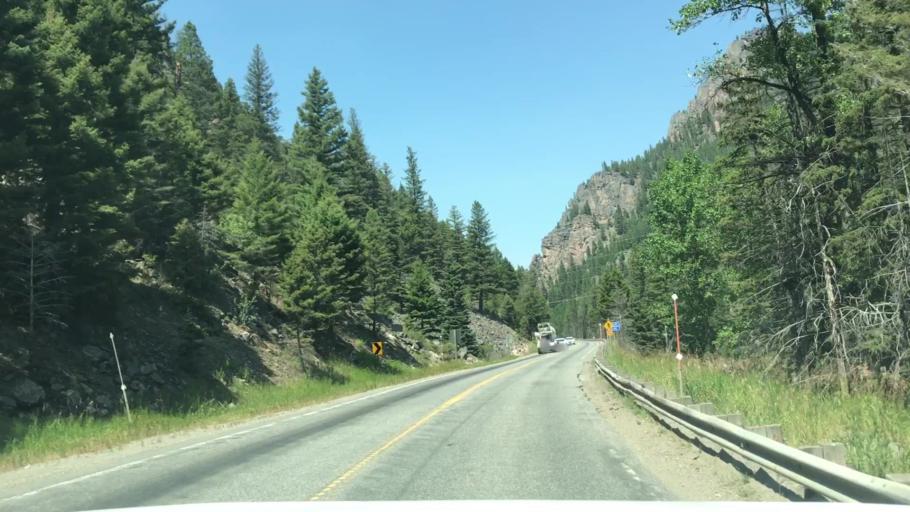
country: US
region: Montana
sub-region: Gallatin County
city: Big Sky
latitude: 45.4085
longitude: -111.2268
